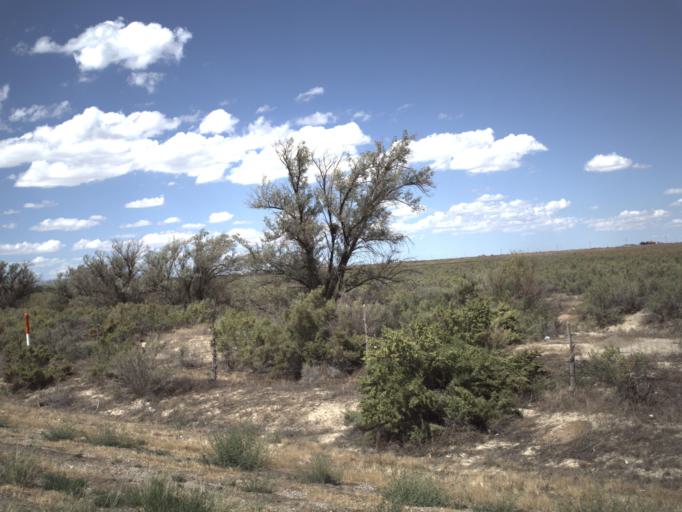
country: US
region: Utah
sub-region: Millard County
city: Delta
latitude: 39.3530
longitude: -112.5274
